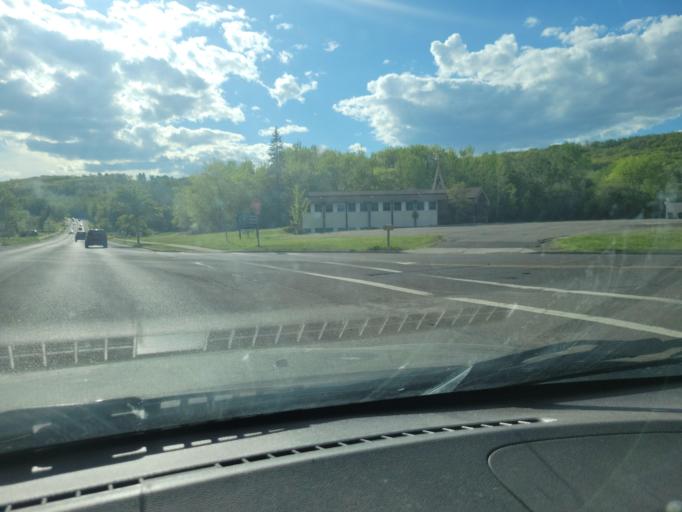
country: US
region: Minnesota
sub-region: Saint Louis County
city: Arnold
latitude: 46.8404
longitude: -92.0313
